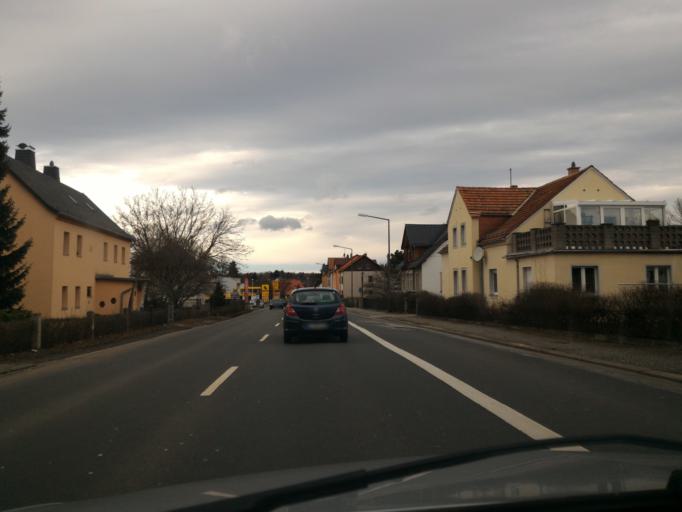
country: DE
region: Saxony
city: Radeberg
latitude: 51.0608
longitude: 13.8593
